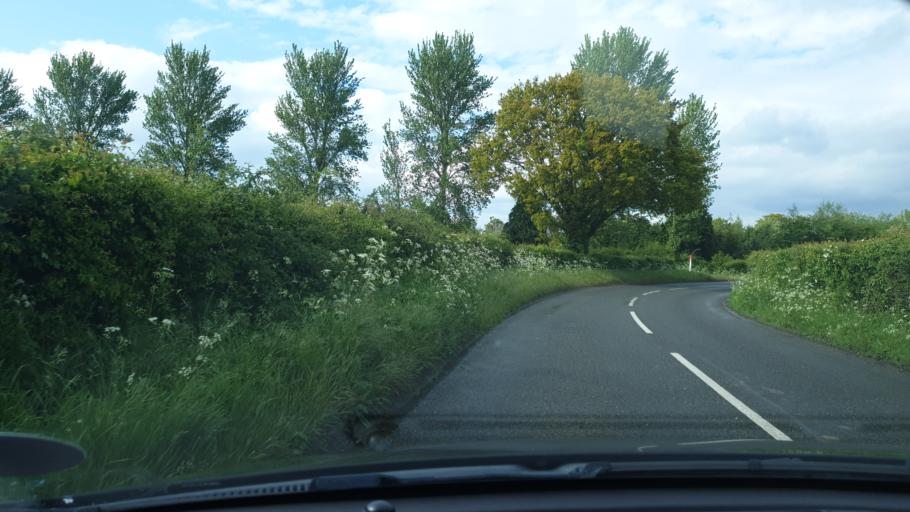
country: GB
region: England
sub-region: Essex
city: Little Clacton
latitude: 51.8289
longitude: 1.1129
